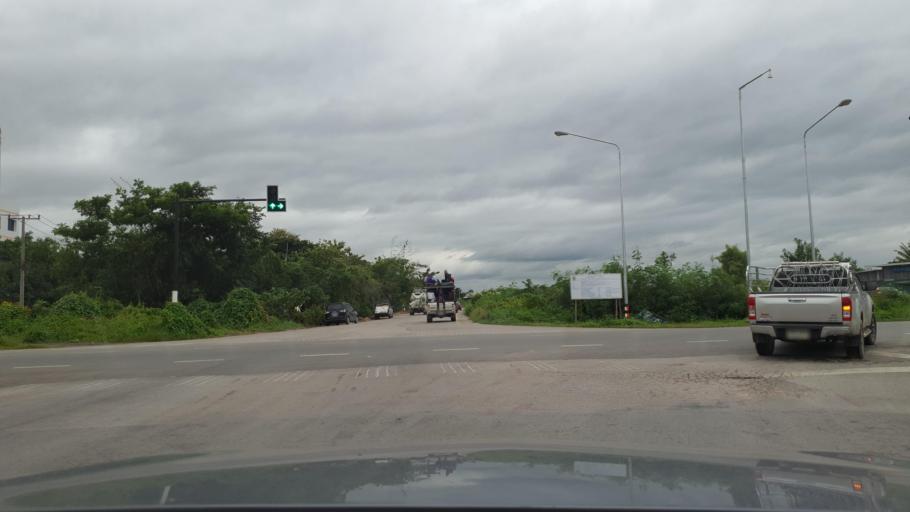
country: TH
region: Lamphun
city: Lamphun
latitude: 18.5840
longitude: 98.9934
